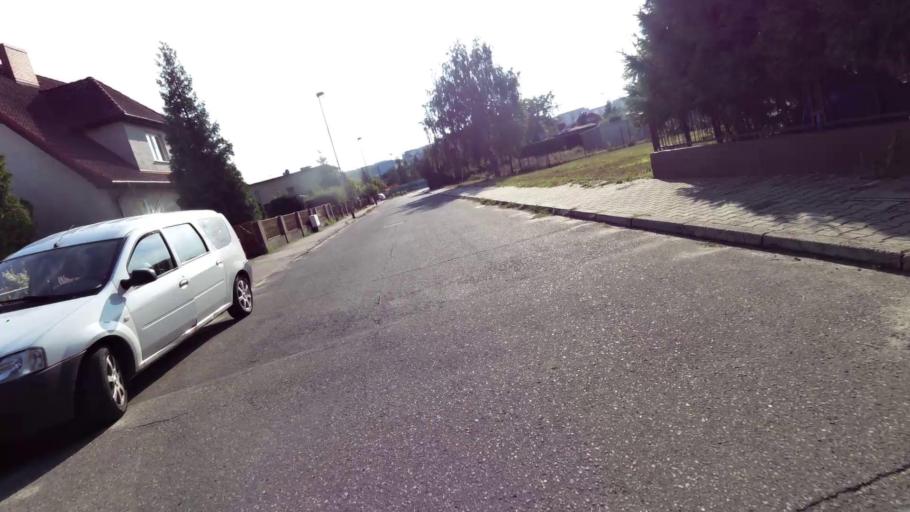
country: PL
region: West Pomeranian Voivodeship
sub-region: Szczecin
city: Szczecin
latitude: 53.3829
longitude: 14.6422
